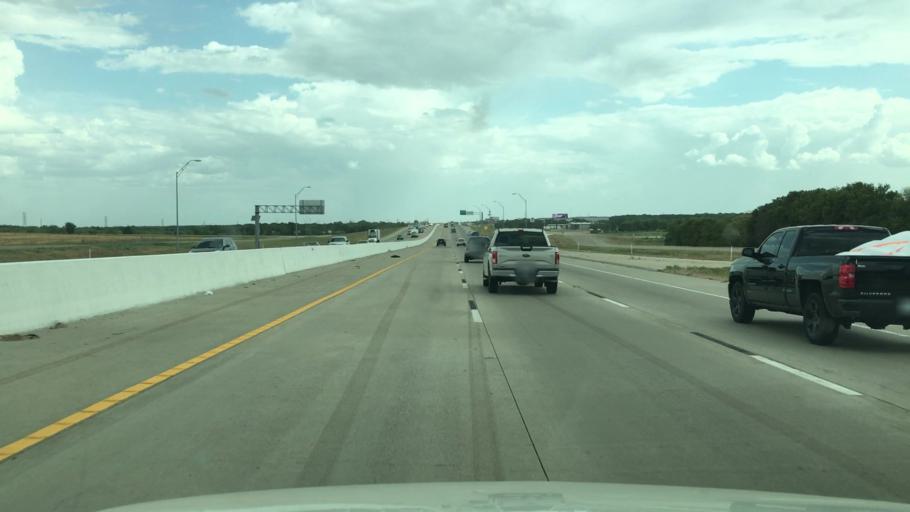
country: US
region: Texas
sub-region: McLennan County
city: West
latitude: 31.7340
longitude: -97.1034
